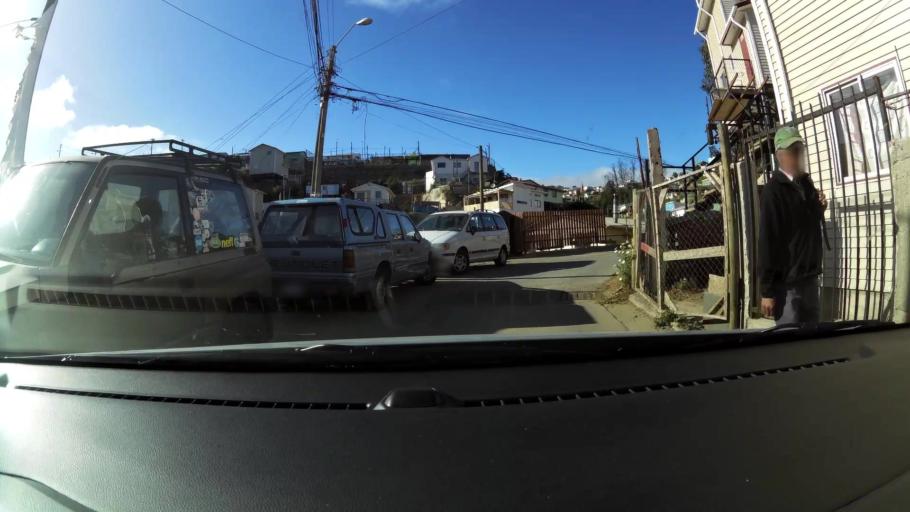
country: CL
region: Valparaiso
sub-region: Provincia de Valparaiso
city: Valparaiso
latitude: -33.0599
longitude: -71.6098
